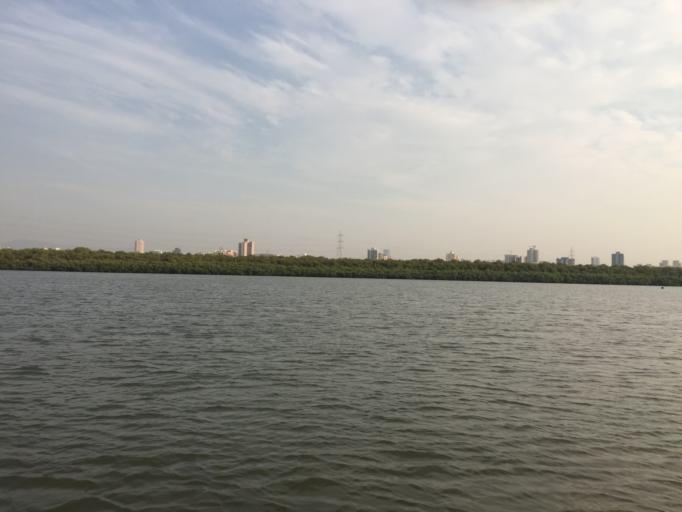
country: IN
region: Maharashtra
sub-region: Mumbai Suburban
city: Borivli
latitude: 19.2272
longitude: 72.8147
